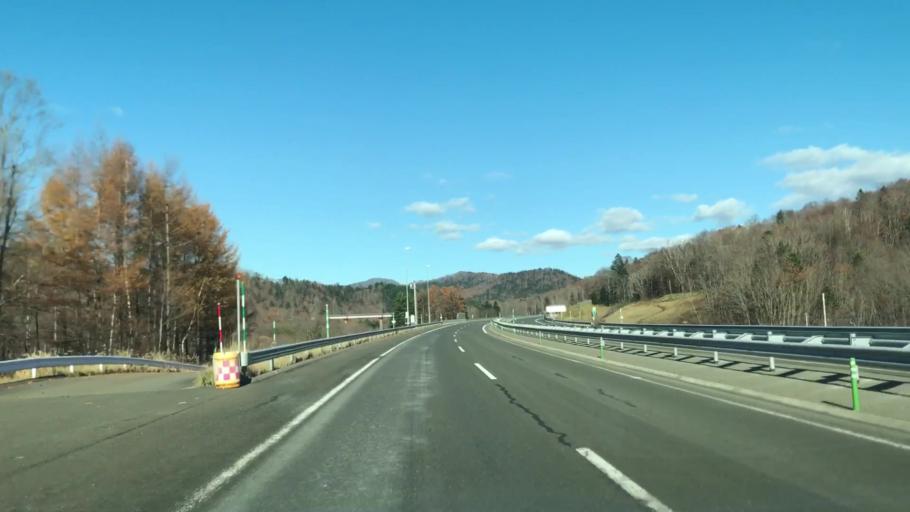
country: JP
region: Hokkaido
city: Shimo-furano
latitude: 42.9333
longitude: 142.2055
